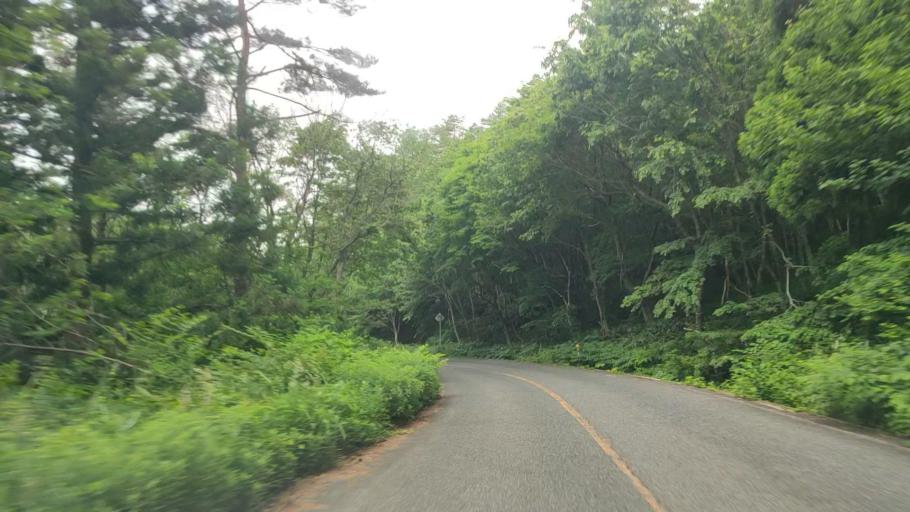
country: JP
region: Tottori
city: Yonago
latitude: 35.3294
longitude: 133.5693
